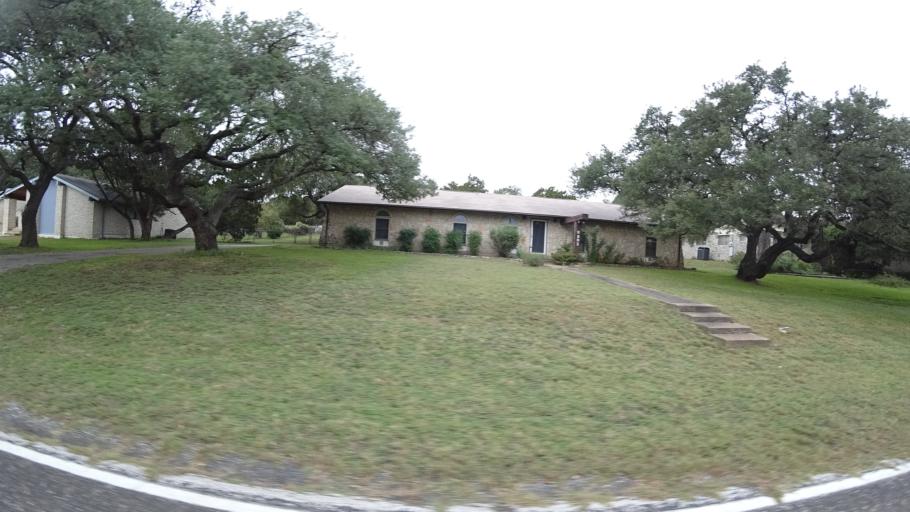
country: US
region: Texas
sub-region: Travis County
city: Barton Creek
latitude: 30.2253
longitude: -97.9010
